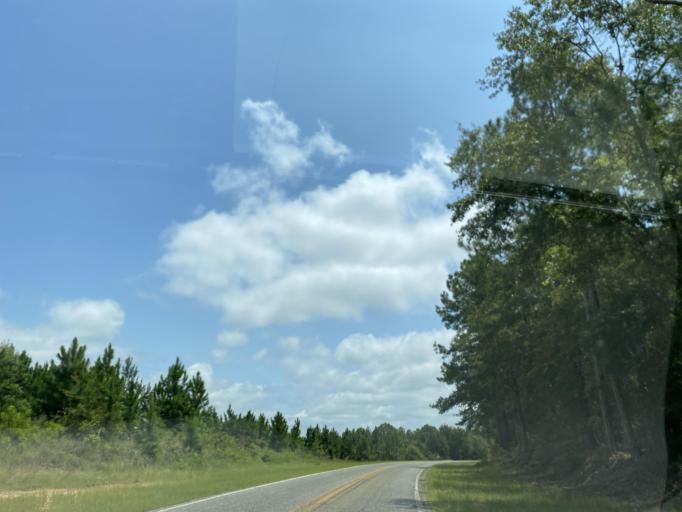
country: US
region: Georgia
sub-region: Wheeler County
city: Alamo
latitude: 32.0789
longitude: -82.7421
